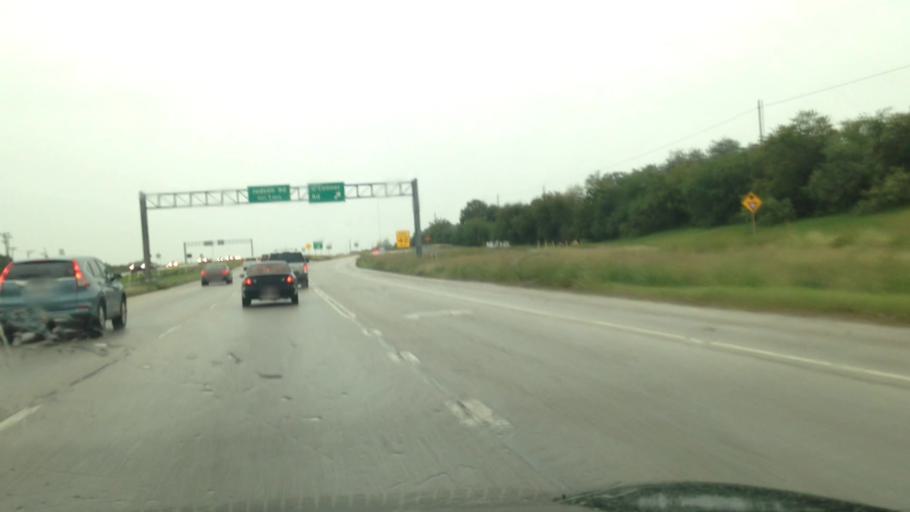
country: US
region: Texas
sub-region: Bexar County
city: Hollywood Park
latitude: 29.6009
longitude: -98.4116
